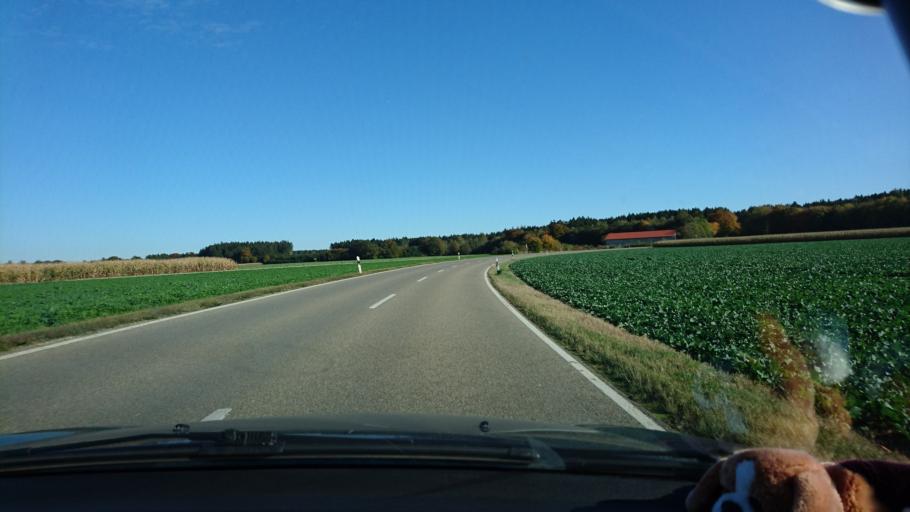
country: DE
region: Bavaria
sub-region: Upper Bavaria
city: Zorneding
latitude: 48.0741
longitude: 11.8320
